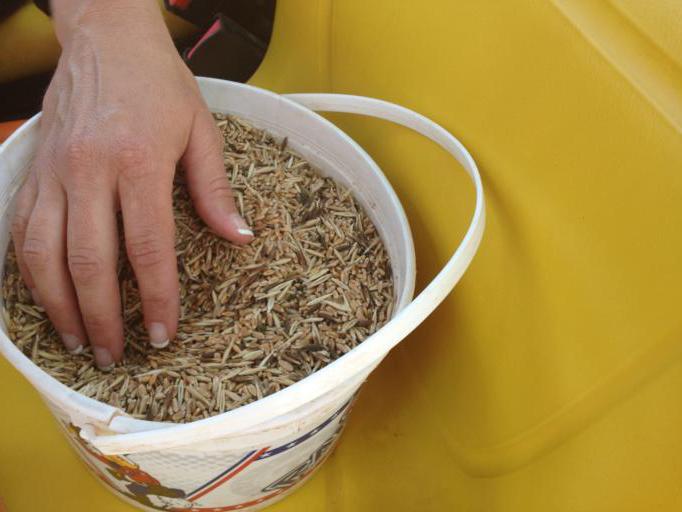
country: US
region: Texas
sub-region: Childress County
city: Childress
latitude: 34.4388
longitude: -100.2220
